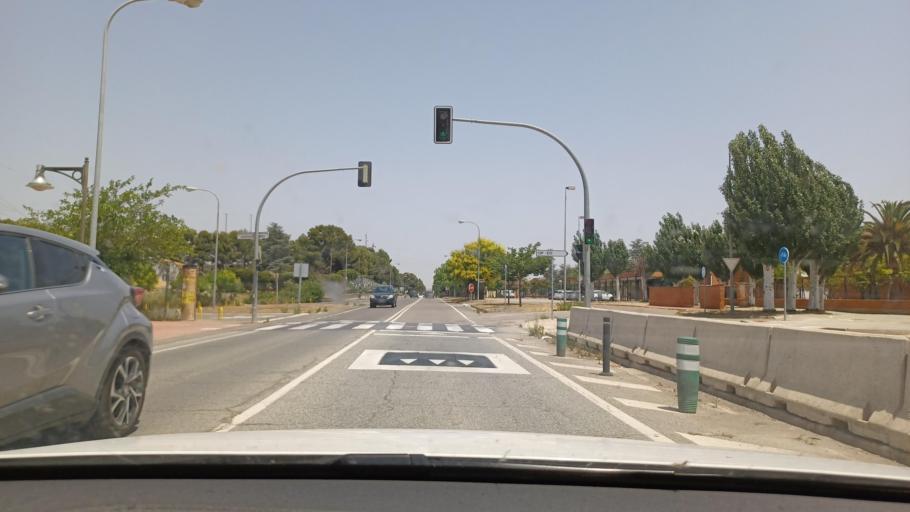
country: ES
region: Navarre
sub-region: Provincia de Navarra
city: Tudela
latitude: 42.0483
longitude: -1.6159
